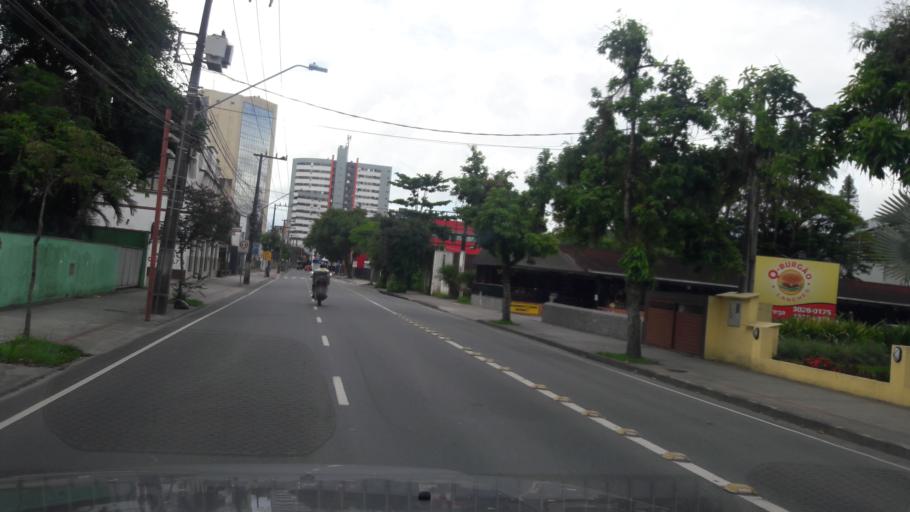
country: BR
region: Santa Catarina
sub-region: Joinville
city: Joinville
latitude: -26.3097
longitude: -48.8429
